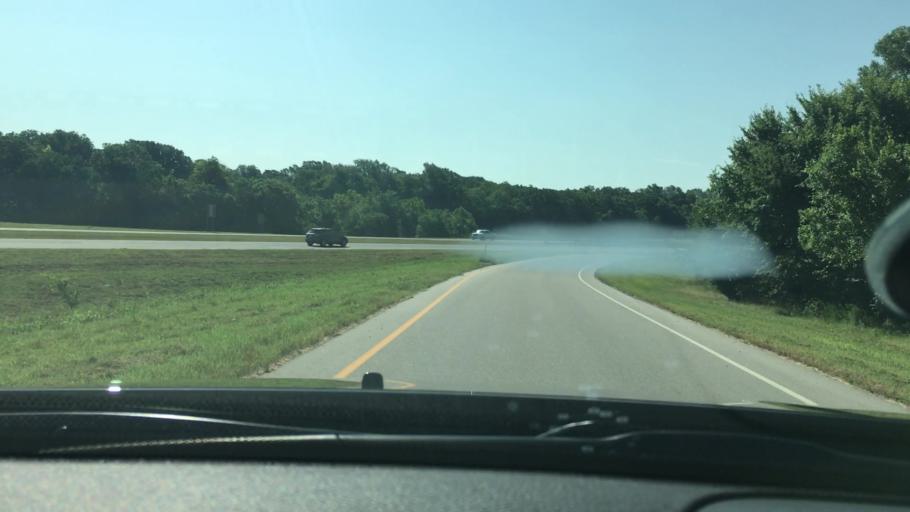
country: US
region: Oklahoma
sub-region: Pontotoc County
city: Ada
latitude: 34.7368
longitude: -96.6448
